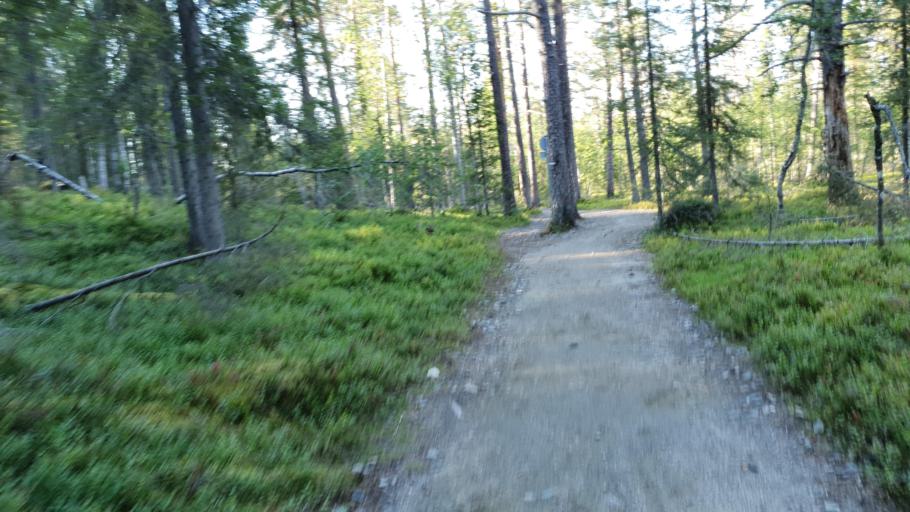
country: FI
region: Lapland
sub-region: Tunturi-Lappi
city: Kolari
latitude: 67.5974
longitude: 24.2170
